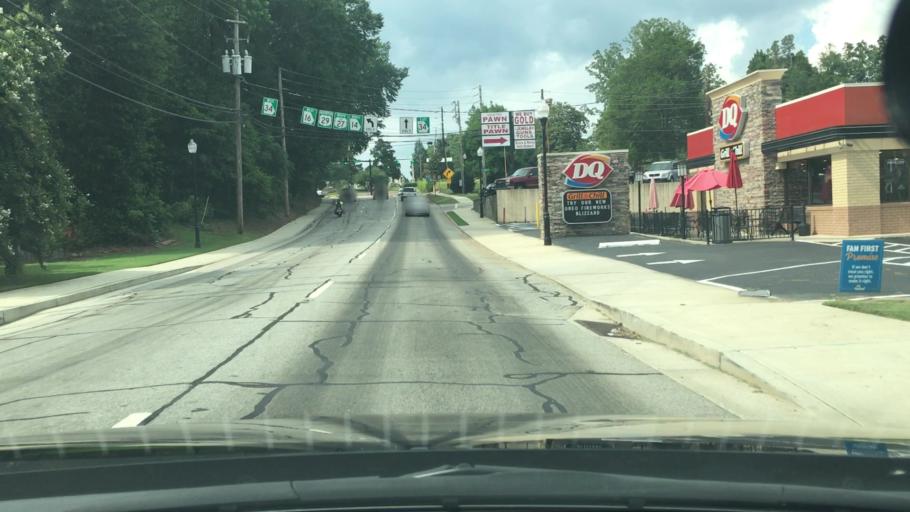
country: US
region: Georgia
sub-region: Coweta County
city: Newnan
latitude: 33.3791
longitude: -84.7990
